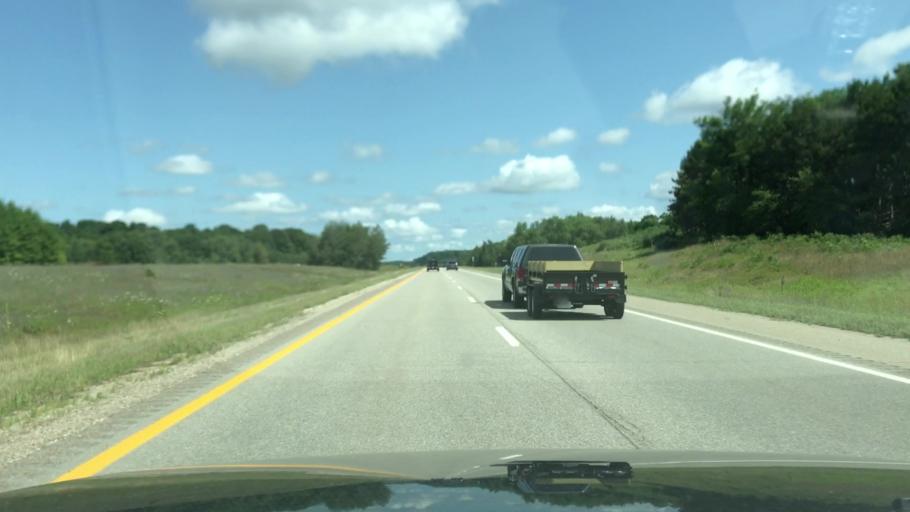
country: US
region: Michigan
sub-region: Mecosta County
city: Big Rapids
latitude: 43.7734
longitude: -85.5343
